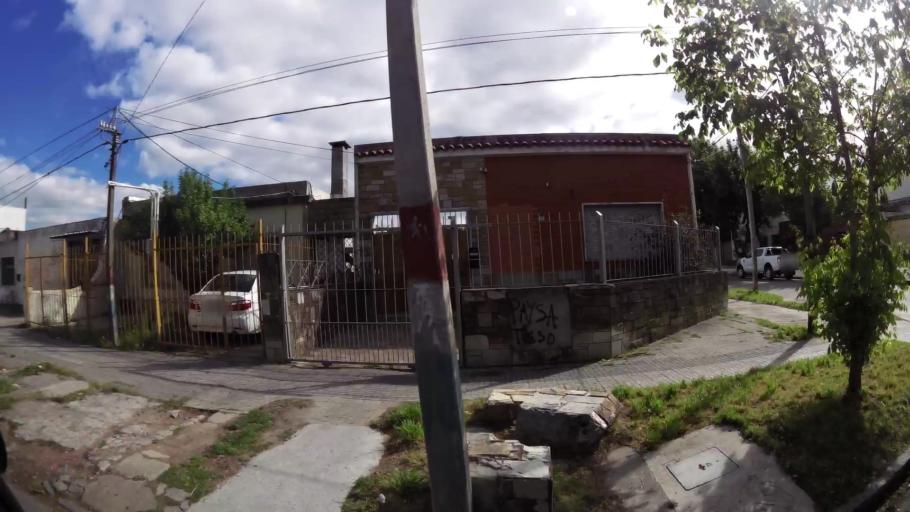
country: UY
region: Montevideo
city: Montevideo
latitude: -34.8792
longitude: -56.1608
